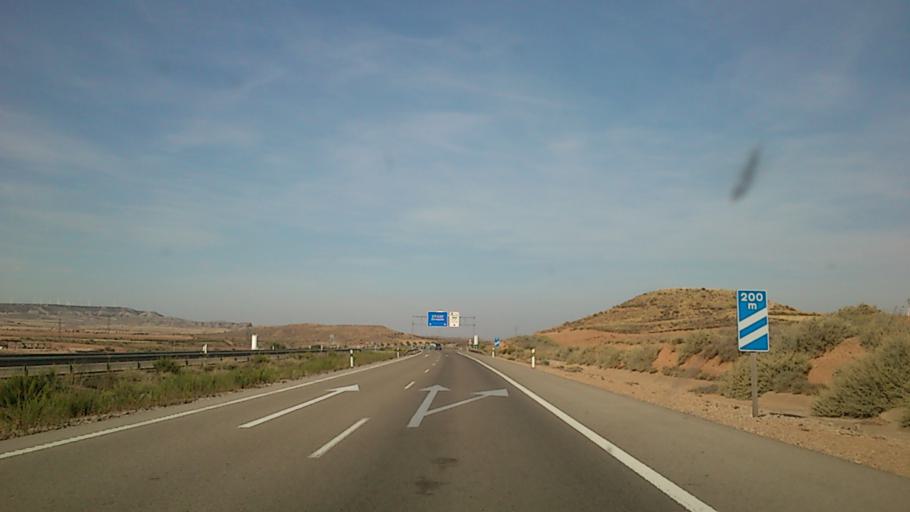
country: ES
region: Aragon
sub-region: Provincia de Zaragoza
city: Muel
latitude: 41.4653
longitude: -1.1043
